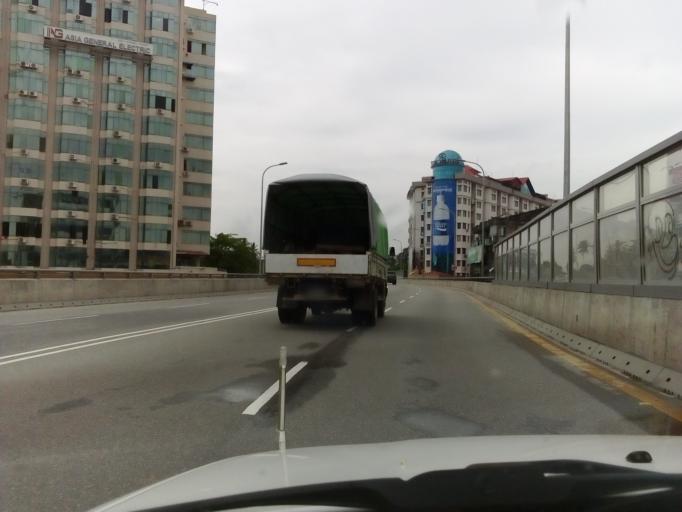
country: MM
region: Yangon
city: Yangon
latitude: 16.8058
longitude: 96.1556
